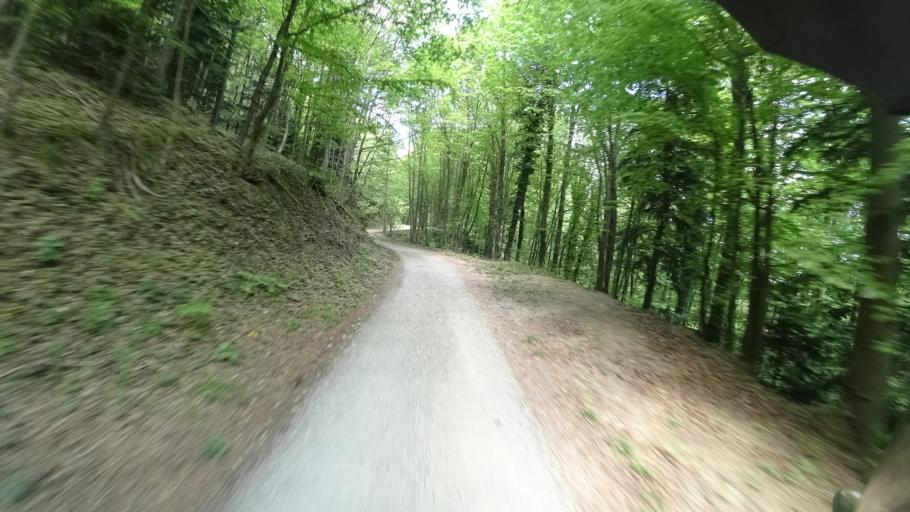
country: HR
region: Grad Zagreb
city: Kasina
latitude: 45.9314
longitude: 16.0305
